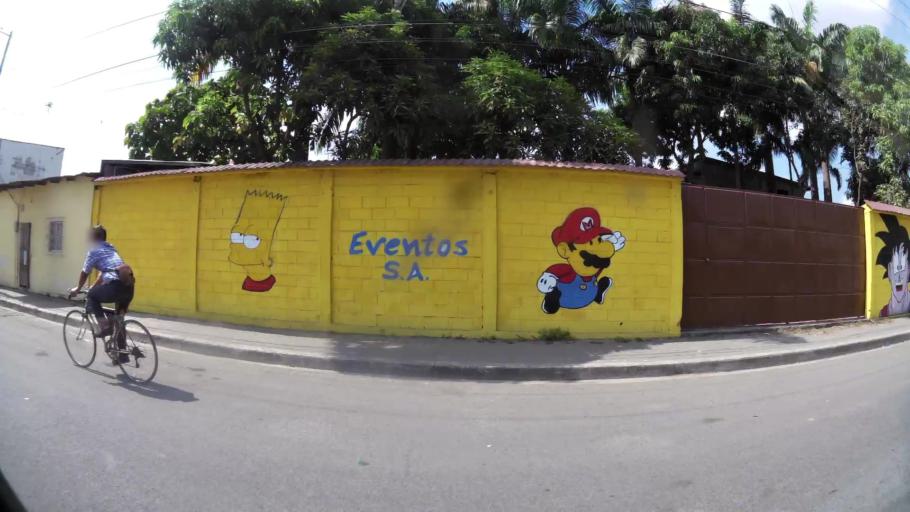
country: EC
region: Guayas
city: Eloy Alfaro
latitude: -2.1570
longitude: -79.8292
